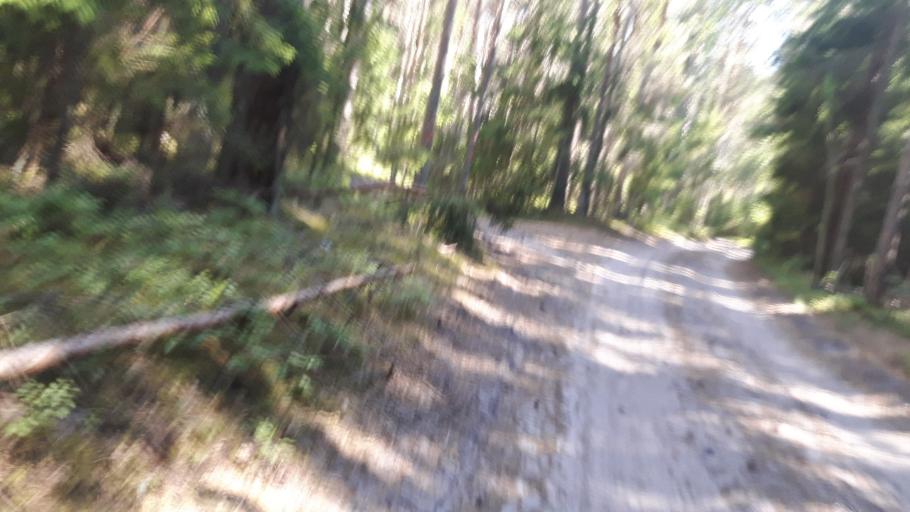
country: LV
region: Salacgrivas
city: Salacgriva
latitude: 57.7231
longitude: 24.3484
